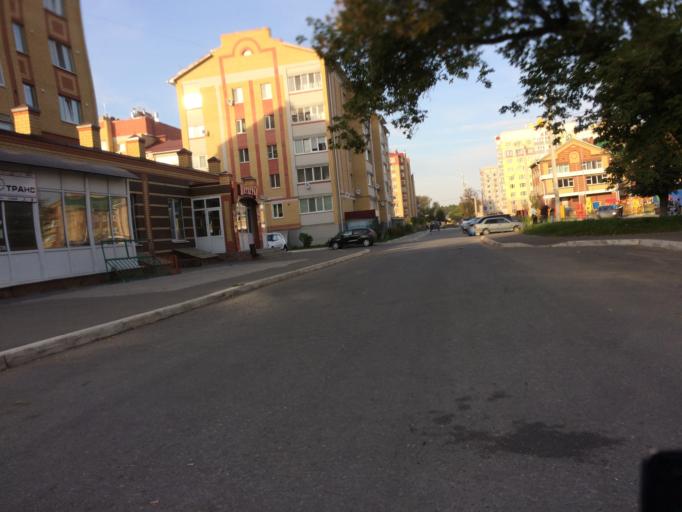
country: RU
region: Mariy-El
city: Yoshkar-Ola
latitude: 56.6276
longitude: 47.8485
